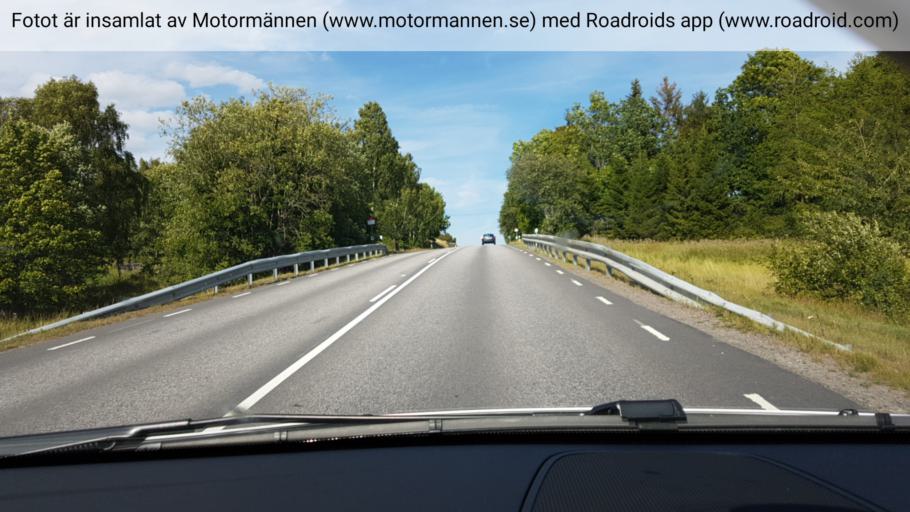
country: SE
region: Stockholm
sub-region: Sodertalje Kommun
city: Pershagen
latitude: 59.0875
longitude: 17.6117
